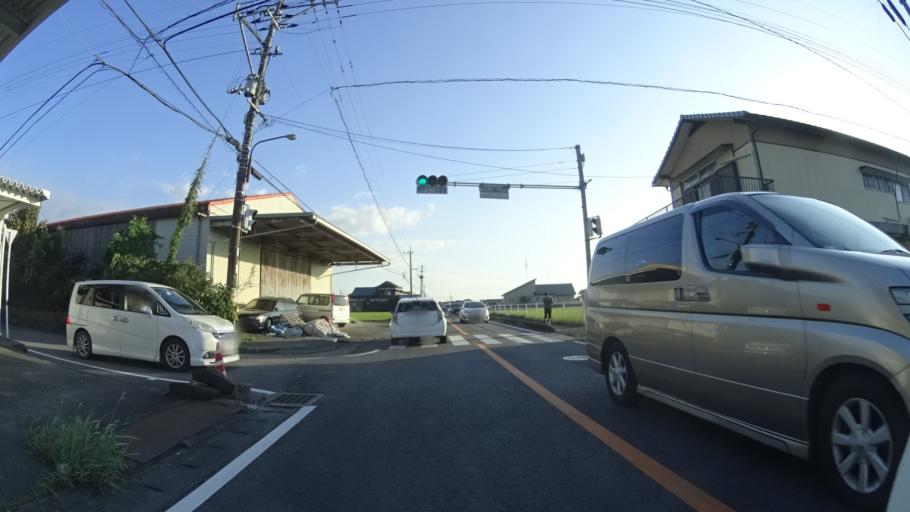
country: JP
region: Kumamoto
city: Matsubase
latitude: 32.5987
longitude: 130.6718
